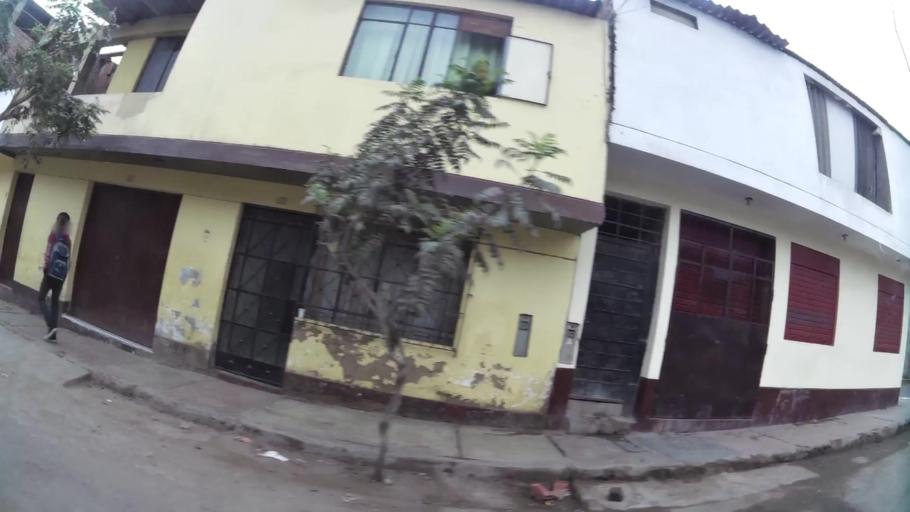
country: PE
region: Lima
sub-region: Lima
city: Surco
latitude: -12.1559
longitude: -76.9570
